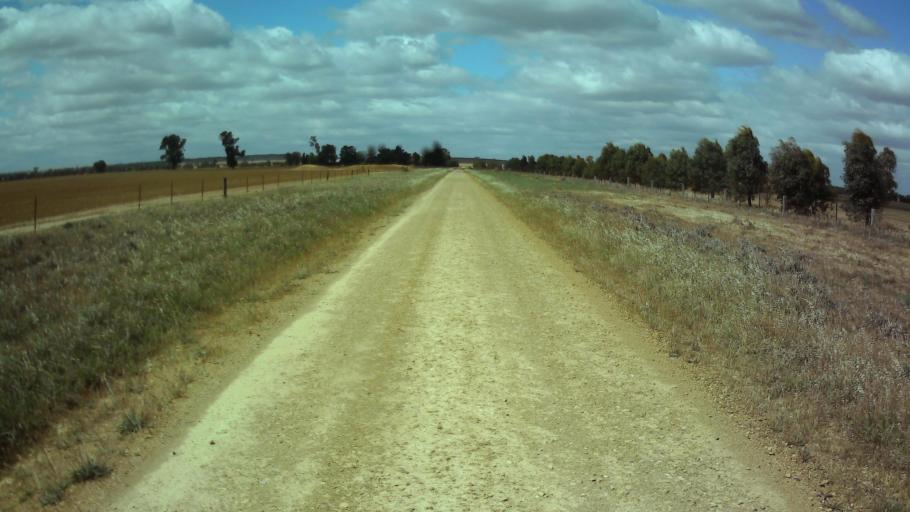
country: AU
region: New South Wales
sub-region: Weddin
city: Grenfell
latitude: -34.0542
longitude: 148.3314
